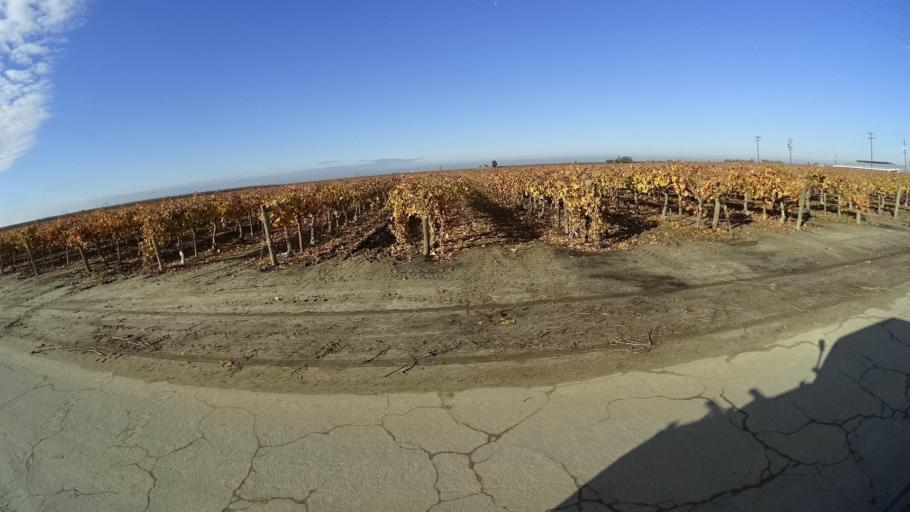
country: US
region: California
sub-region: Kern County
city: McFarland
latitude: 35.7059
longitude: -119.3030
